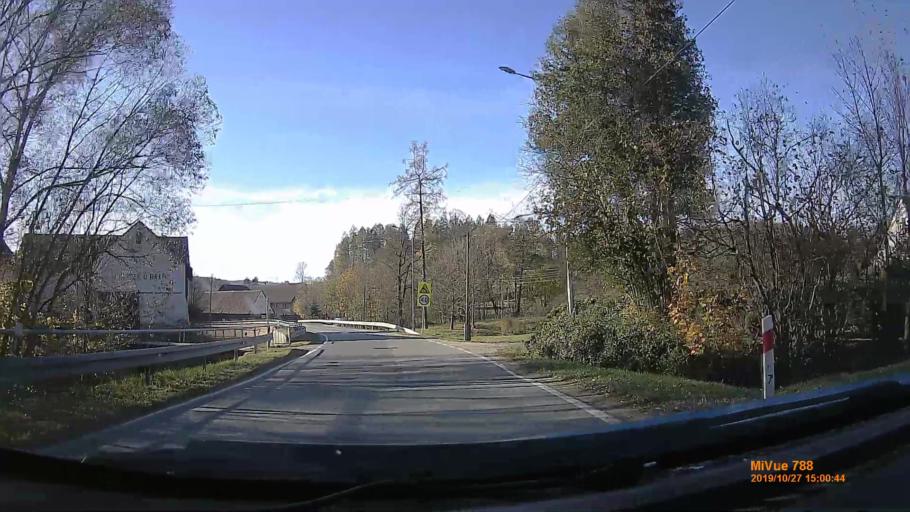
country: PL
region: Lower Silesian Voivodeship
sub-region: Powiat klodzki
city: Miedzylesie
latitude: 50.1187
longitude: 16.6845
